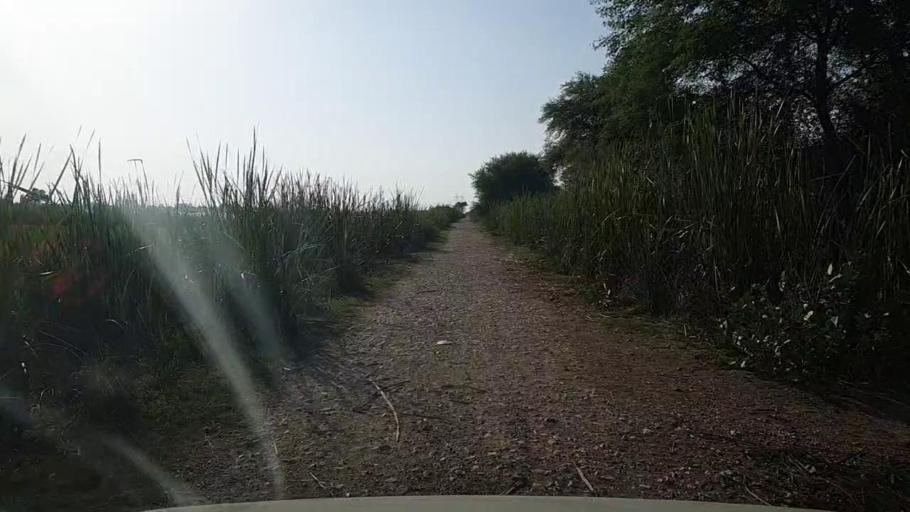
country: PK
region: Sindh
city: Kandhkot
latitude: 28.2889
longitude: 69.3289
